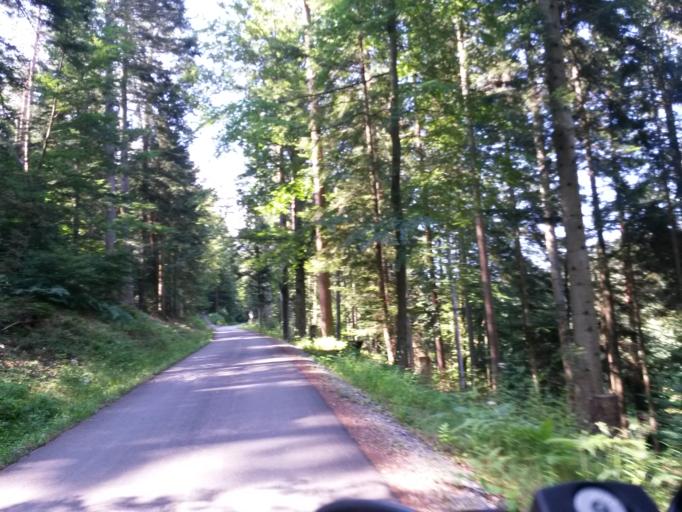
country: DE
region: Baden-Wuerttemberg
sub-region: Karlsruhe Region
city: Enzklosterle
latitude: 48.6726
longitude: 8.4779
